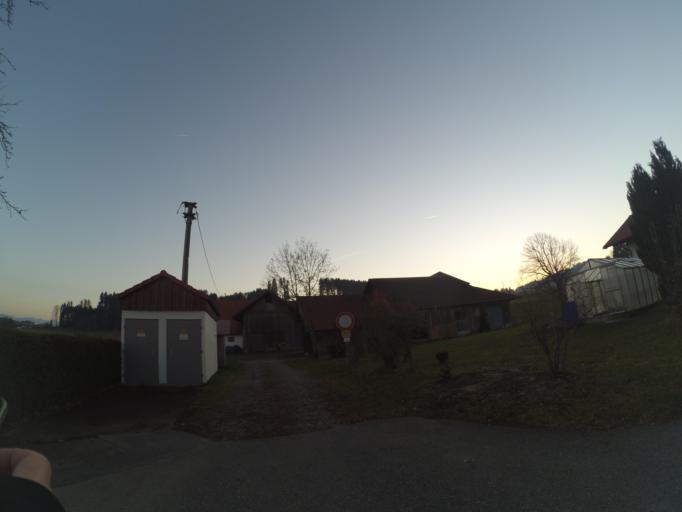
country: DE
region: Bavaria
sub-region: Upper Bavaria
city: Bernbeuren
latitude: 47.7390
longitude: 10.7701
